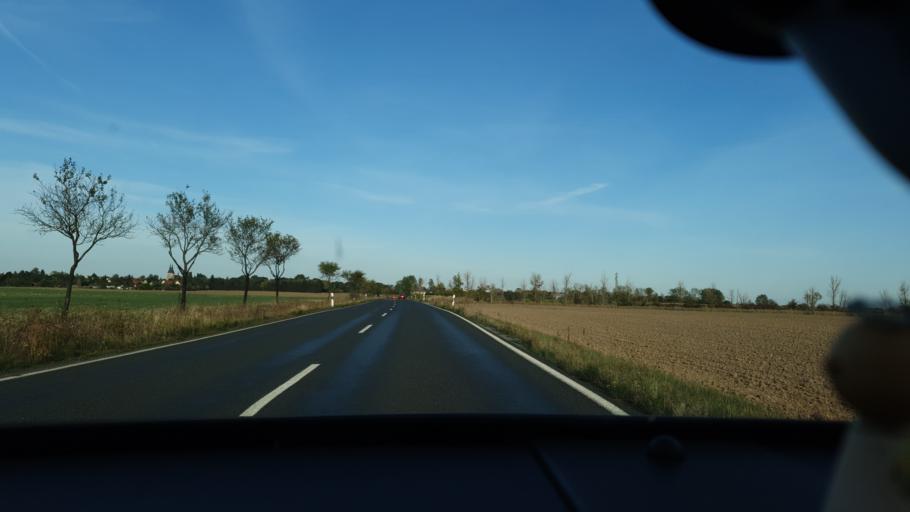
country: DE
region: Saxony
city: Krostitz
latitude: 51.4557
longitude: 12.4381
